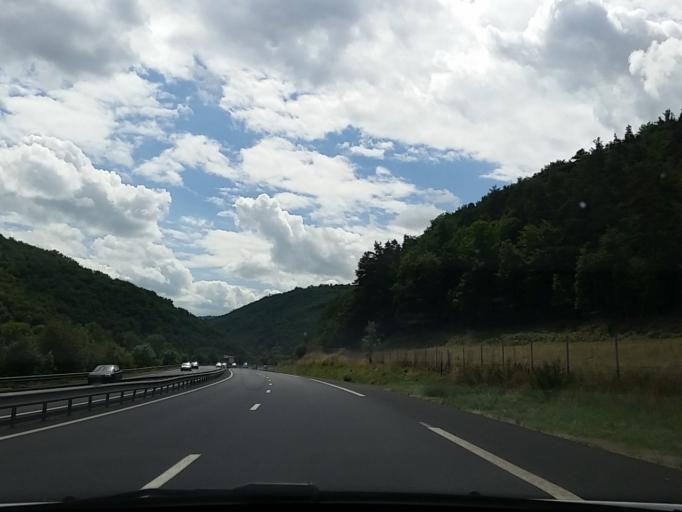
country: FR
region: Auvergne
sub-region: Departement du Cantal
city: Massiac
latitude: 45.2300
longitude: 3.2065
